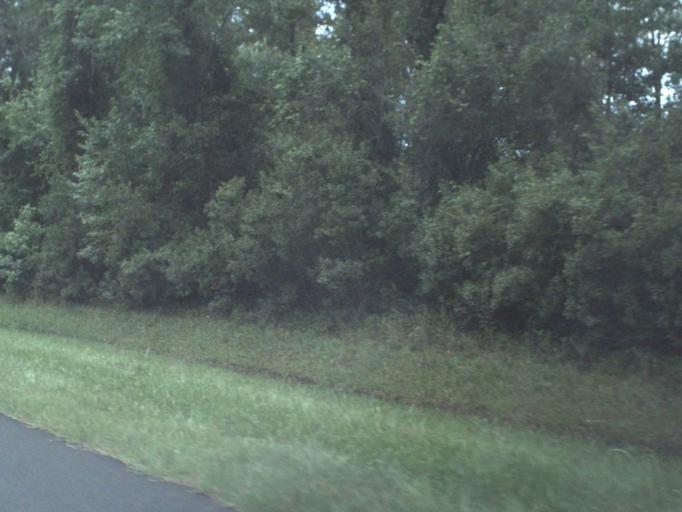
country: US
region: Florida
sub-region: Union County
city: Lake Butler
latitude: 30.0609
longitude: -82.4241
